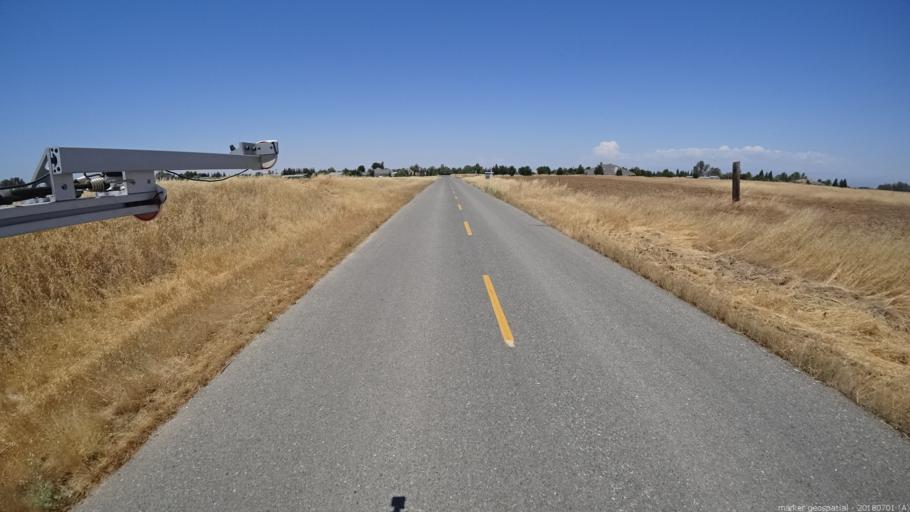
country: US
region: California
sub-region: Madera County
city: Madera Acres
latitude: 37.0633
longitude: -120.0158
